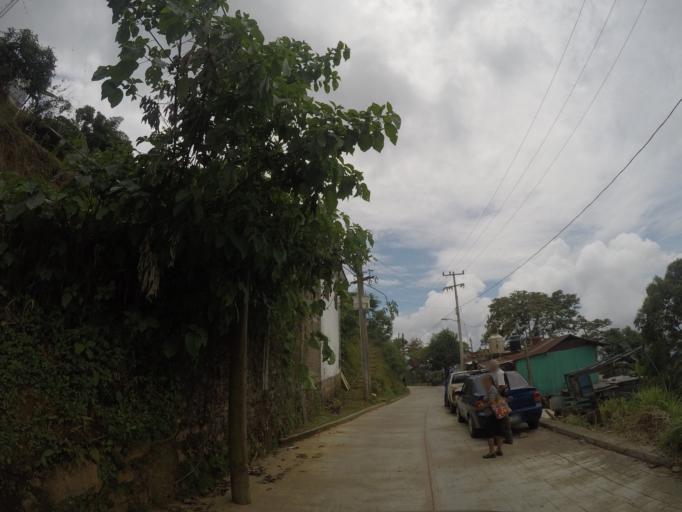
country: MX
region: Oaxaca
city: Pluma Hidalgo
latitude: 15.9233
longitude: -96.4182
